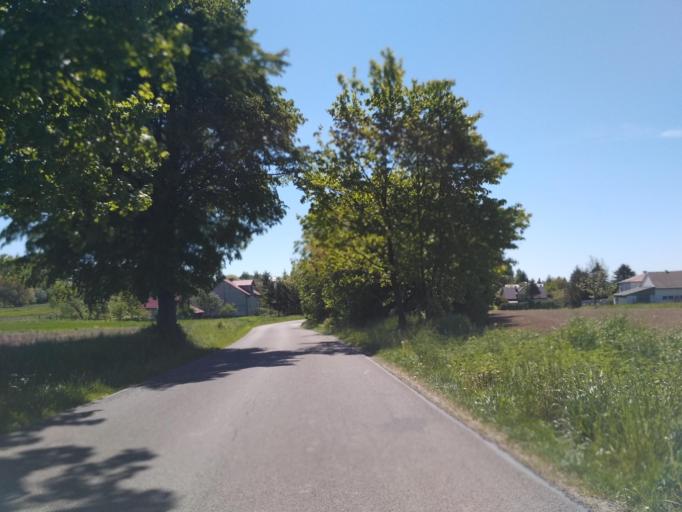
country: PL
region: Subcarpathian Voivodeship
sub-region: Powiat brzozowski
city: Turze Pole
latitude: 49.6416
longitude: 21.9943
